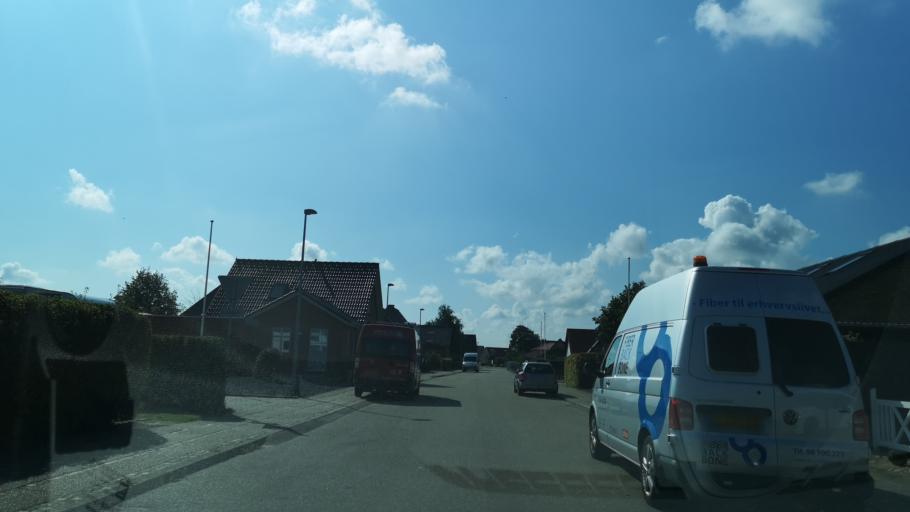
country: DK
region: Central Jutland
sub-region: Ringkobing-Skjern Kommune
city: Skjern
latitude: 55.9519
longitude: 8.4974
